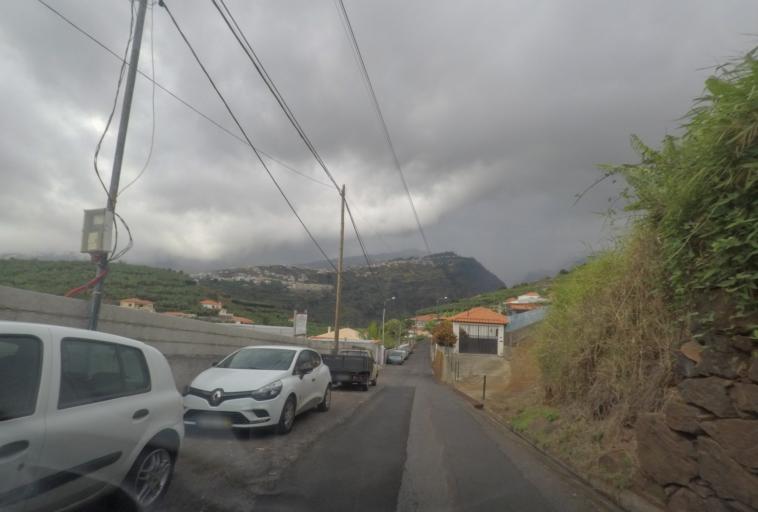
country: PT
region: Madeira
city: Camara de Lobos
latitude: 32.6581
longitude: -16.9559
